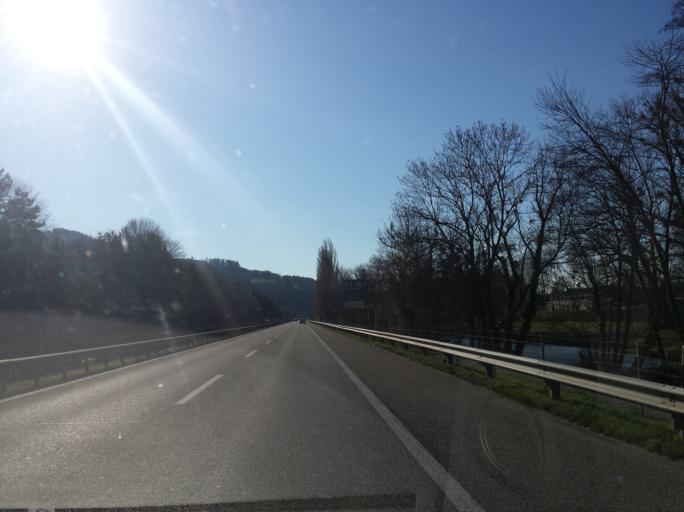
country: CH
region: Saint Gallen
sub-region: Wahlkreis Rheintal
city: Sankt Margrethen
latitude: 47.4561
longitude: 9.6355
